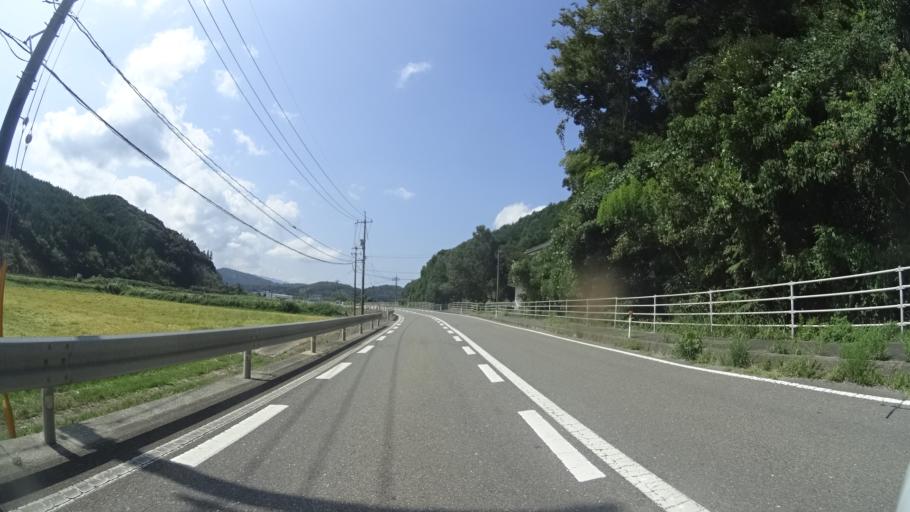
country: JP
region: Shimane
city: Masuda
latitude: 34.6543
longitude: 131.6712
